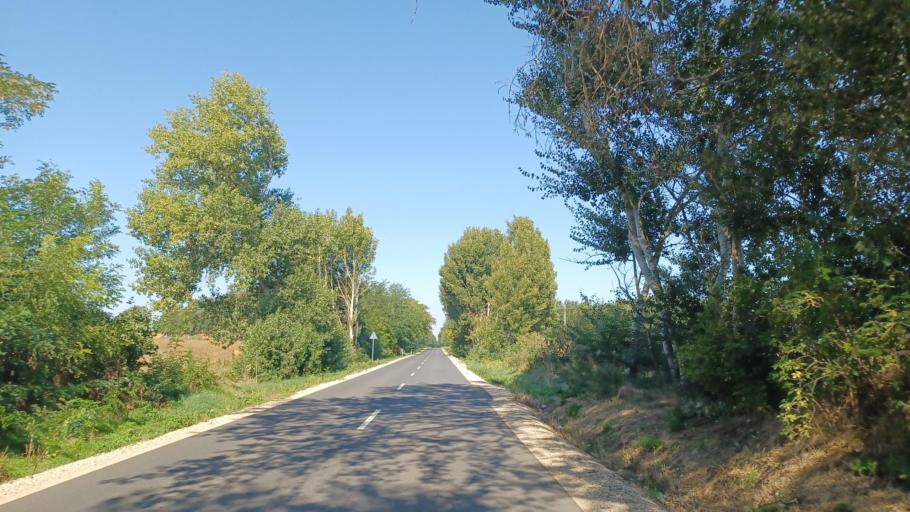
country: HU
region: Fejer
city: Cece
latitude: 46.7534
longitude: 18.6681
